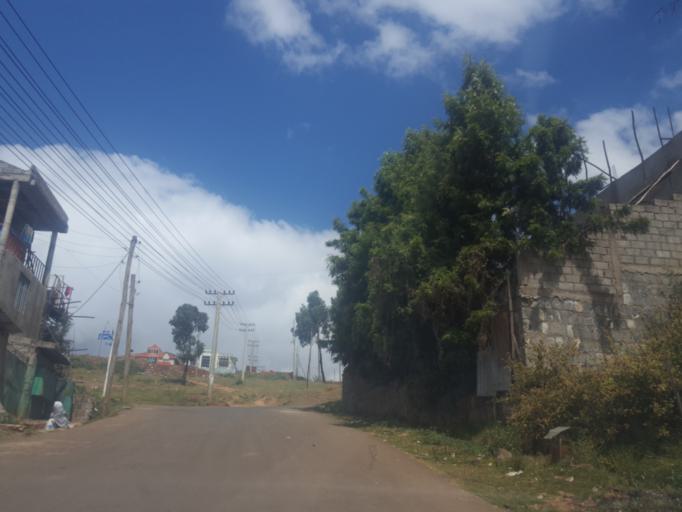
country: ET
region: Adis Abeba
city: Addis Ababa
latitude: 9.0661
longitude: 38.7418
